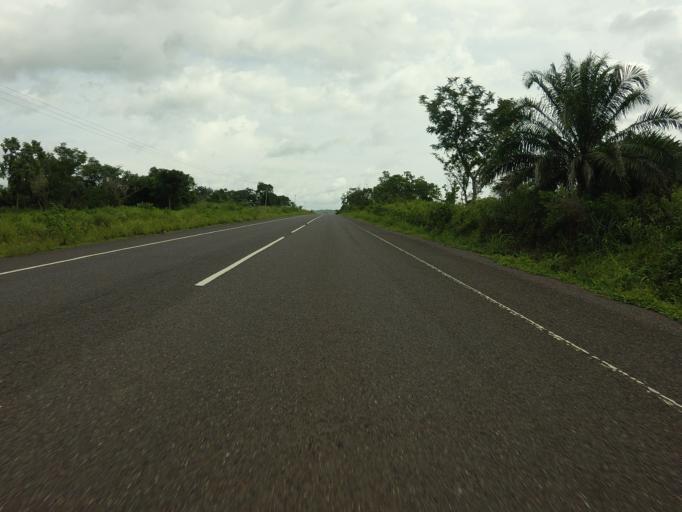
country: TG
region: Plateaux
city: Badou
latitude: 7.9694
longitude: 0.5580
